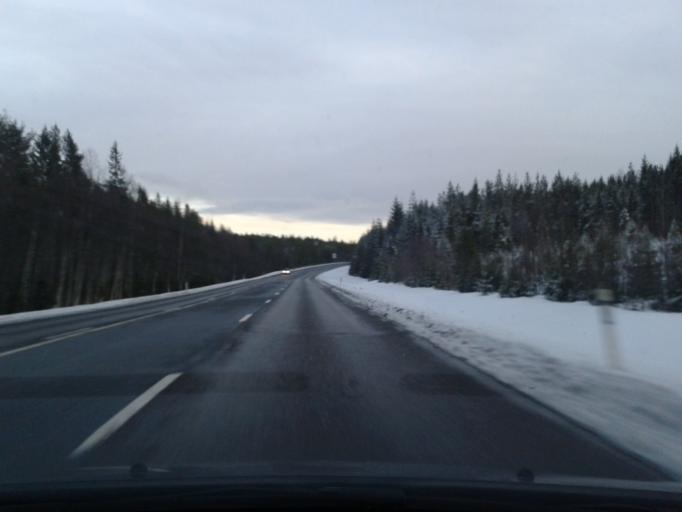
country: SE
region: Vaesternorrland
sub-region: Solleftea Kommun
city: Solleftea
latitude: 63.1270
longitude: 17.4810
